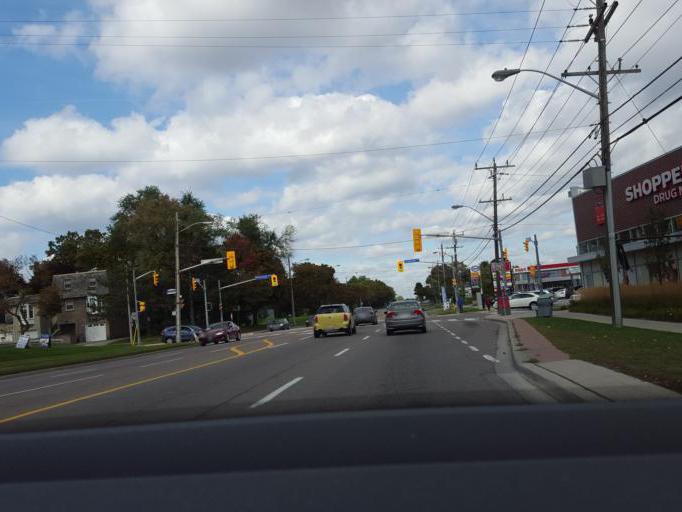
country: CA
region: Ontario
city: Willowdale
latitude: 43.7544
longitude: -79.3602
